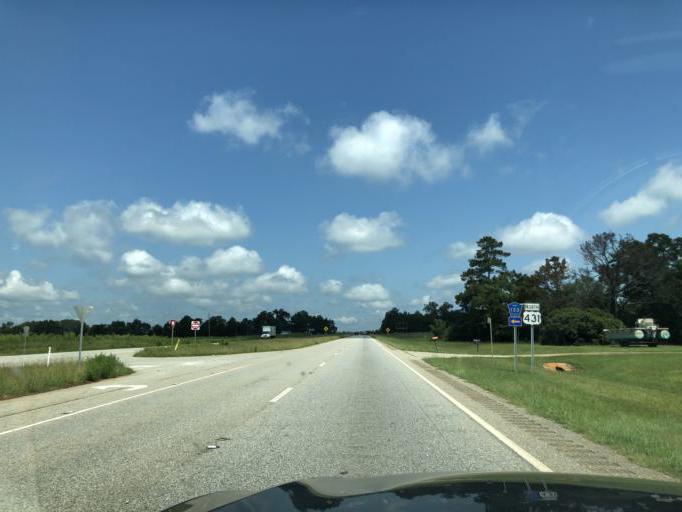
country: US
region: Alabama
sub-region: Henry County
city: Abbeville
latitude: 31.6166
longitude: -85.2774
